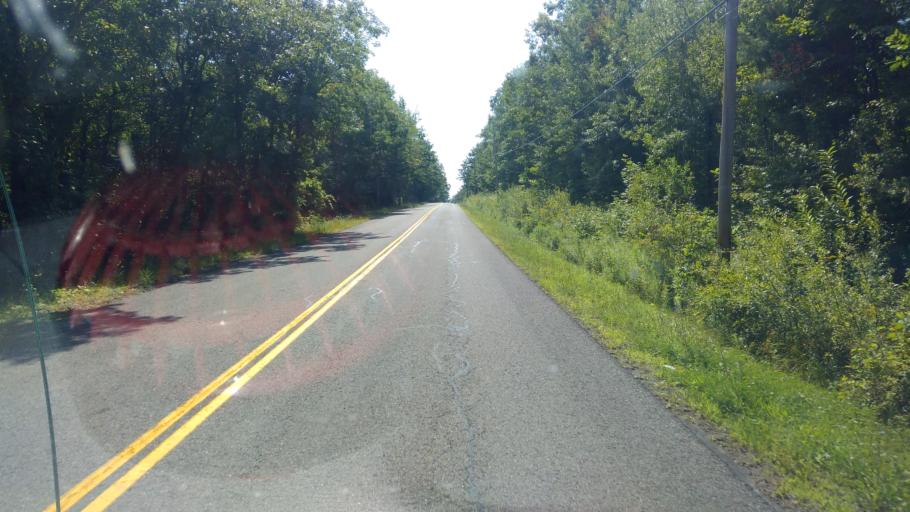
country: US
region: New York
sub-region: Allegany County
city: Belmont
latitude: 42.2889
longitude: -77.9966
